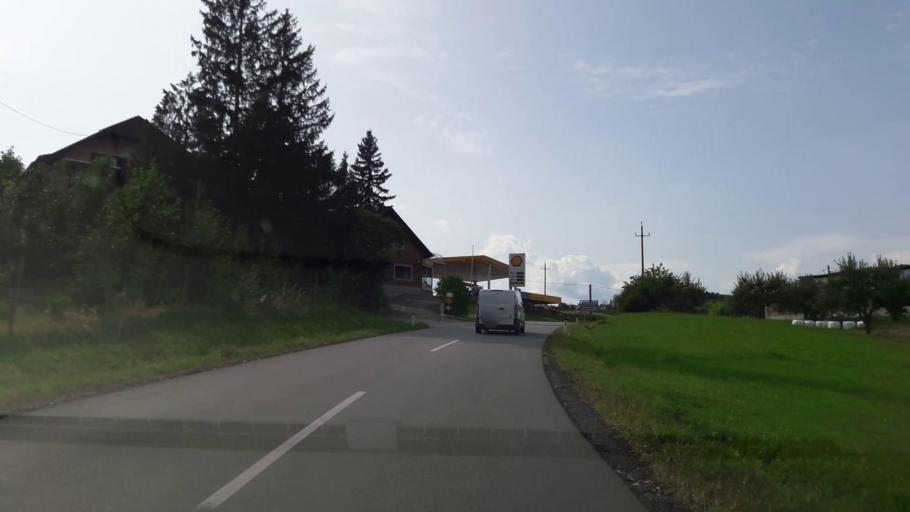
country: AT
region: Styria
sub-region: Politischer Bezirk Hartberg-Fuerstenfeld
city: Kaibing
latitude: 47.2340
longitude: 15.8371
